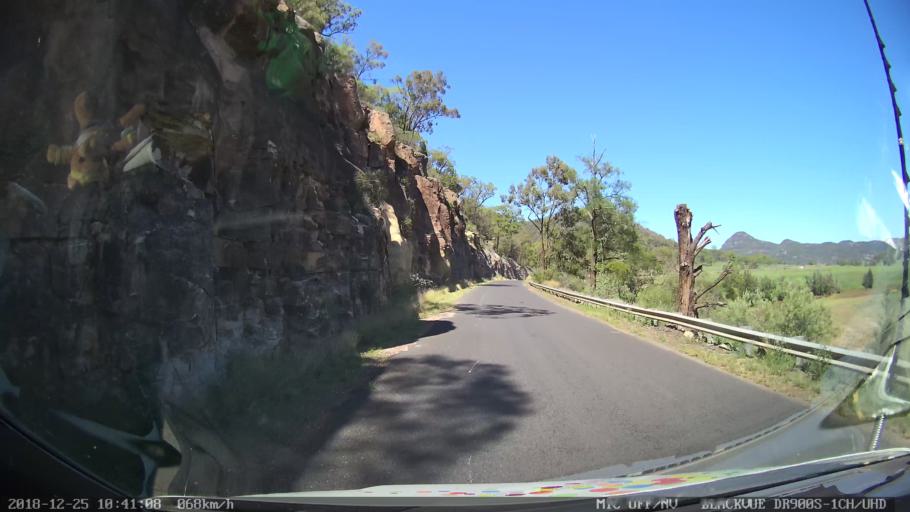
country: AU
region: New South Wales
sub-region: Upper Hunter Shire
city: Merriwa
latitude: -32.4145
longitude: 150.3382
